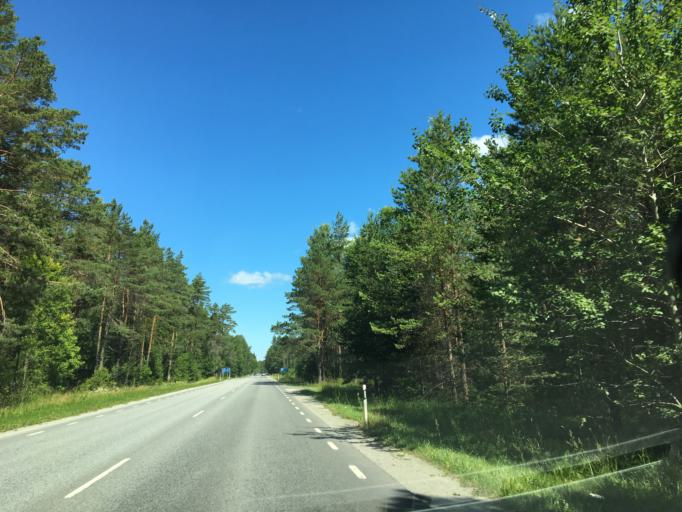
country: EE
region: Harju
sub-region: Nissi vald
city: Riisipere
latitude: 59.2422
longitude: 24.2771
